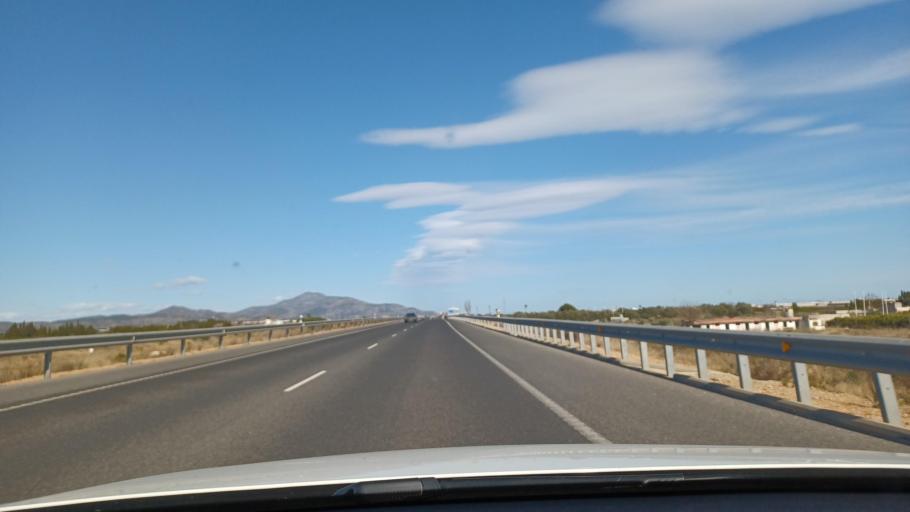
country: ES
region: Valencia
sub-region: Provincia de Castello
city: Vinaros
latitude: 40.4855
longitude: 0.4519
